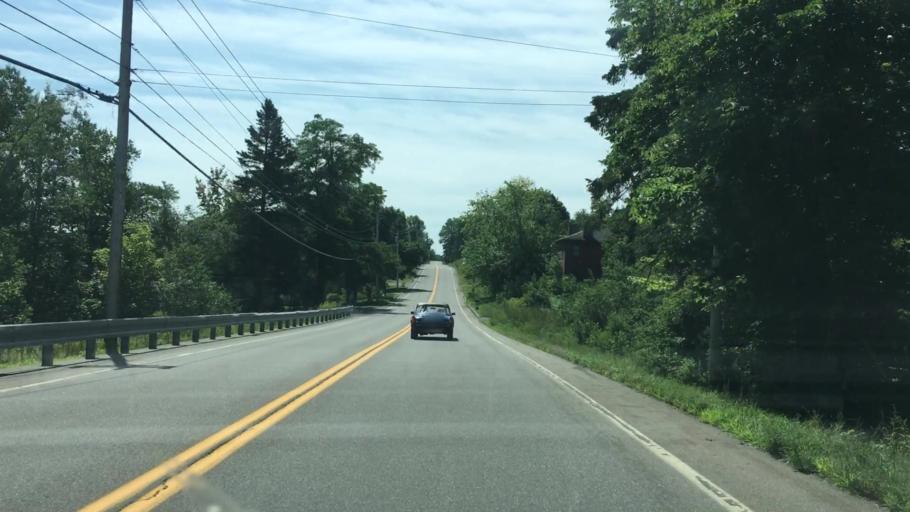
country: CA
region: New Brunswick
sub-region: Charlotte County
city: Saint Andrews
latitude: 45.0818
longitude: -67.1104
